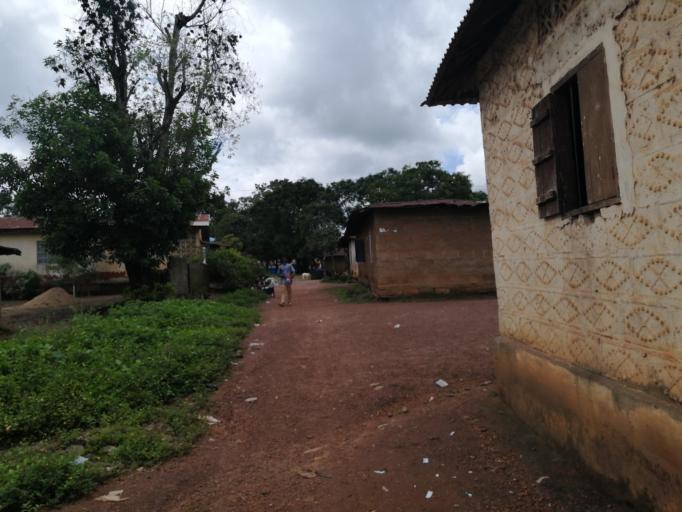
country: SL
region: Northern Province
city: Port Loko
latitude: 8.7714
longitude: -12.7878
